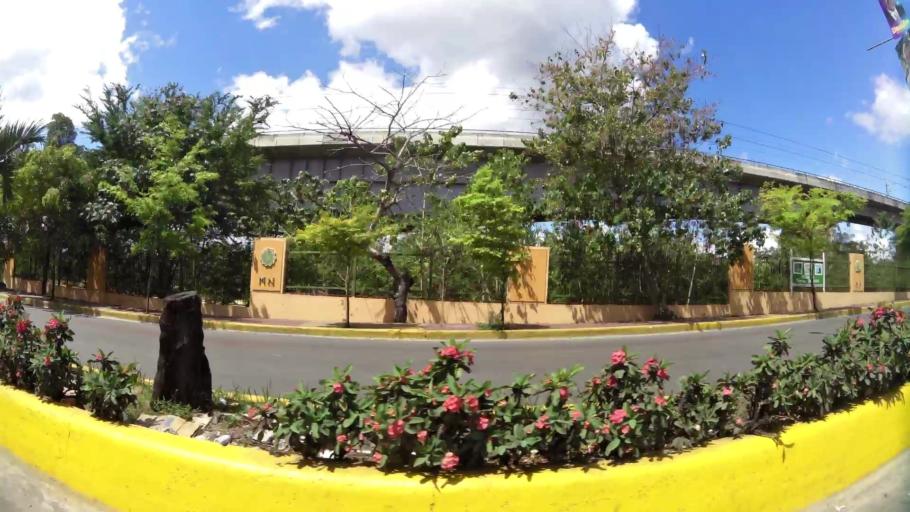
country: DO
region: Nacional
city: Ensanche Luperon
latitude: 18.5163
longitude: -69.9149
